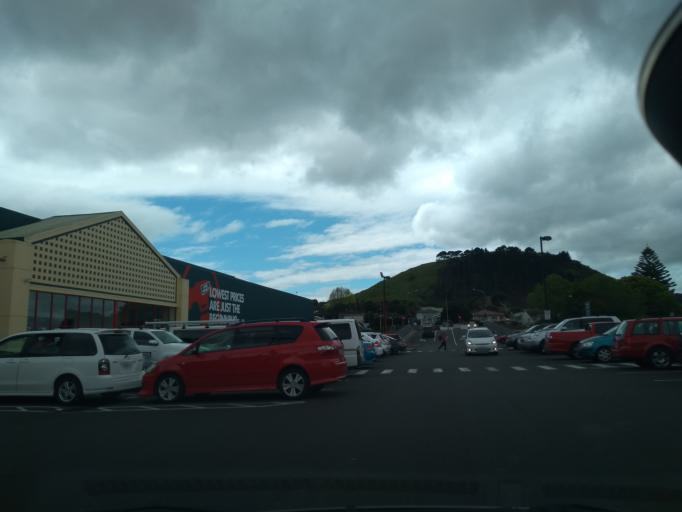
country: NZ
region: Auckland
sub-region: Auckland
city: Tamaki
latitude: -36.8983
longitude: 174.8424
